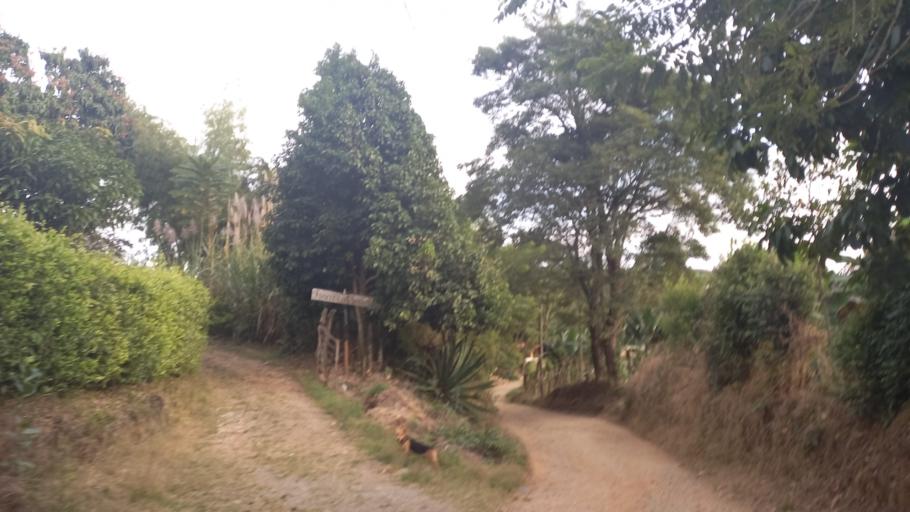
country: CO
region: Antioquia
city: Santa Barbara
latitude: 5.8185
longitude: -75.5722
